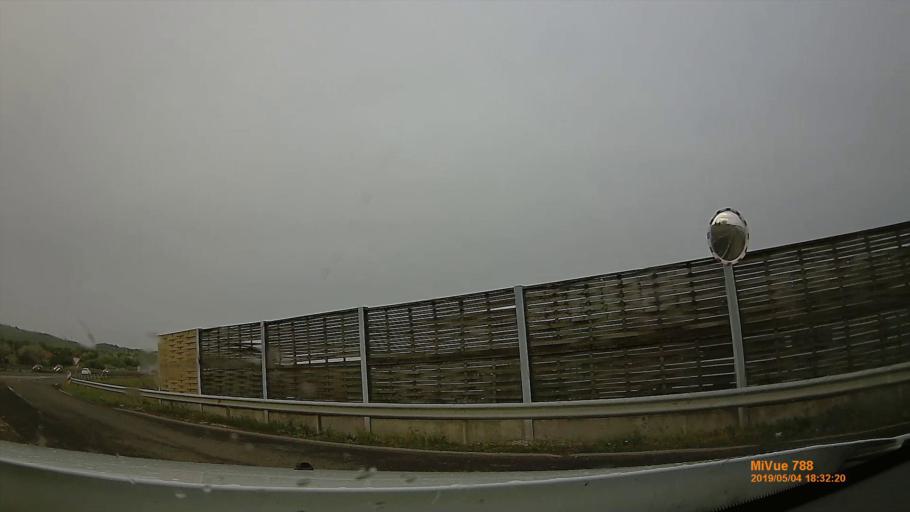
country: HU
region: Pest
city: Biatorbagy
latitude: 47.4939
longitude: 18.8202
